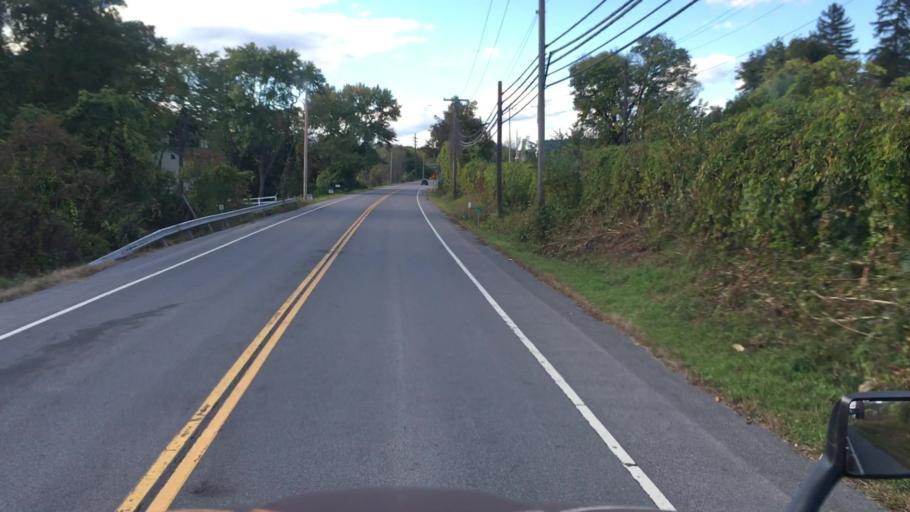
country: US
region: New York
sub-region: Schenectady County
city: Scotia
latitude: 42.8321
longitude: -73.9812
